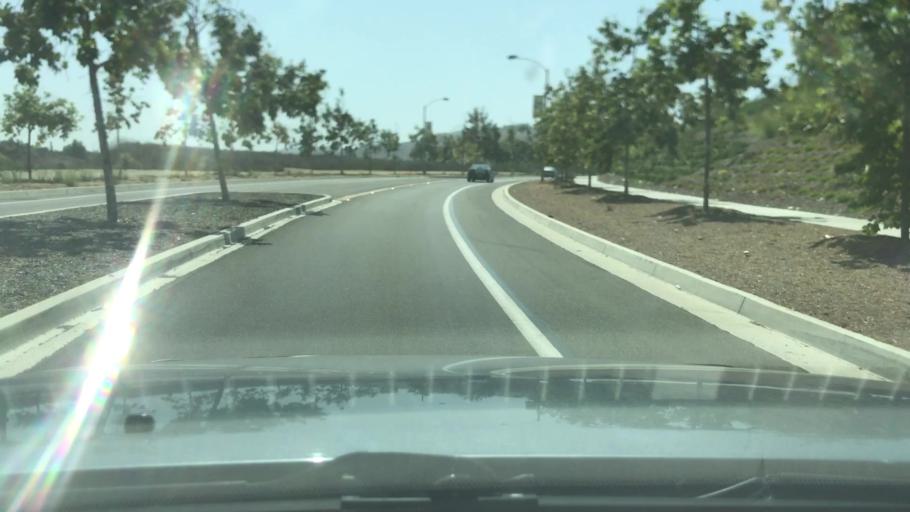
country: US
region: California
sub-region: Orange County
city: San Joaquin Hills
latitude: 33.6384
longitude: -117.8291
